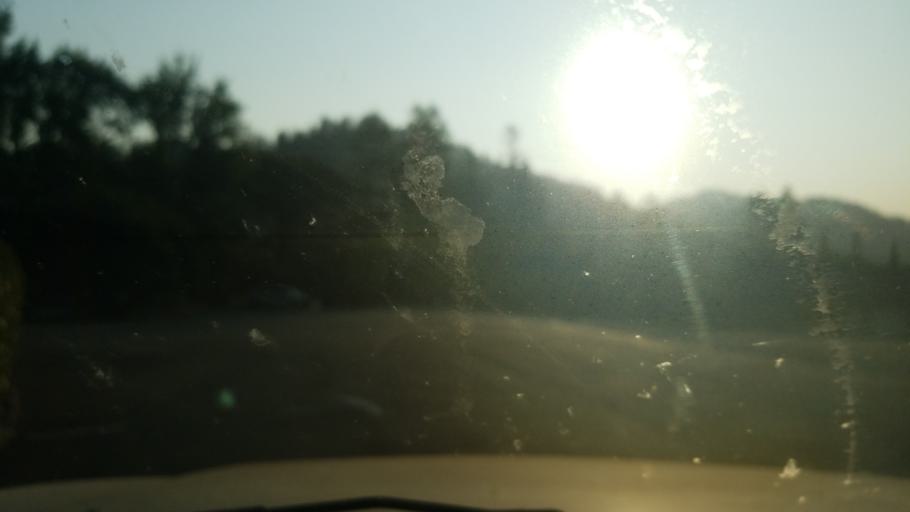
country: US
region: California
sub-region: Humboldt County
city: Redway
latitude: 40.0671
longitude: -123.7898
